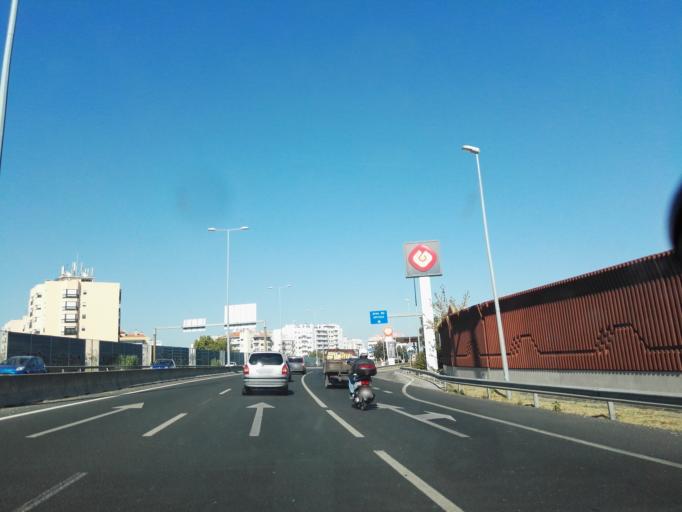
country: PT
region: Lisbon
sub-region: Odivelas
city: Olival do Basto
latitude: 38.7667
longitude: -9.1722
